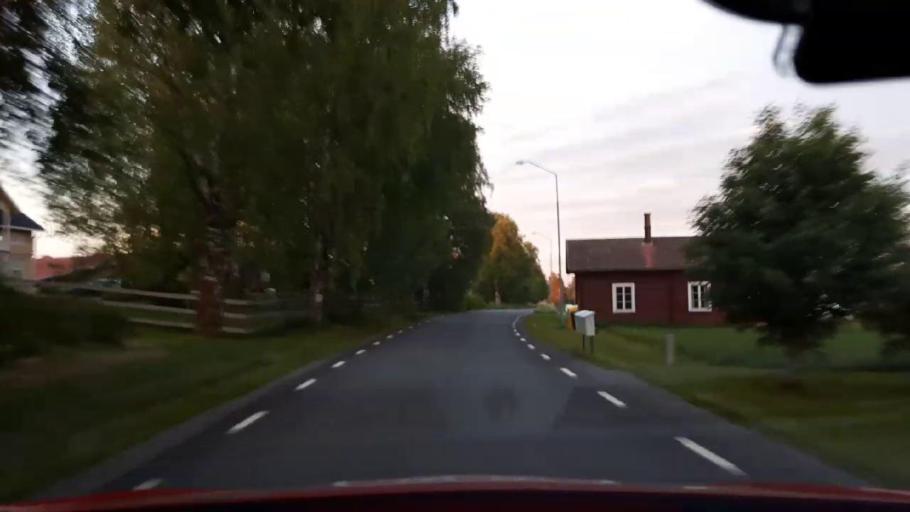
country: SE
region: Jaemtland
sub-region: OEstersunds Kommun
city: Brunflo
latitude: 63.0565
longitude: 14.8136
